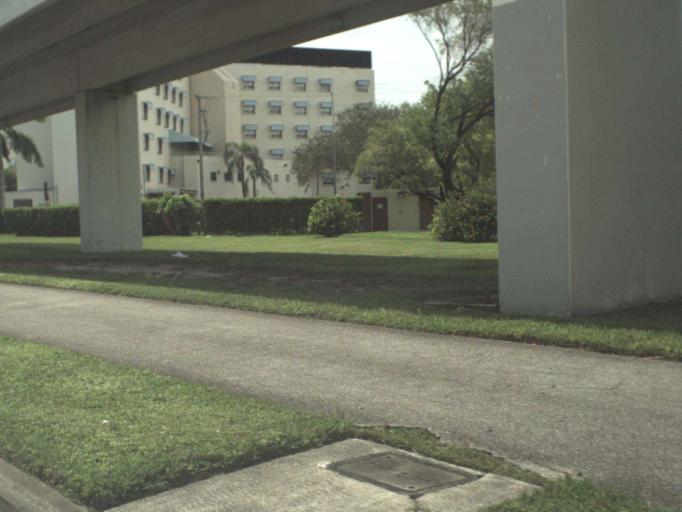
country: US
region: Florida
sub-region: Miami-Dade County
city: South Miami
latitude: 25.7028
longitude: -80.2917
